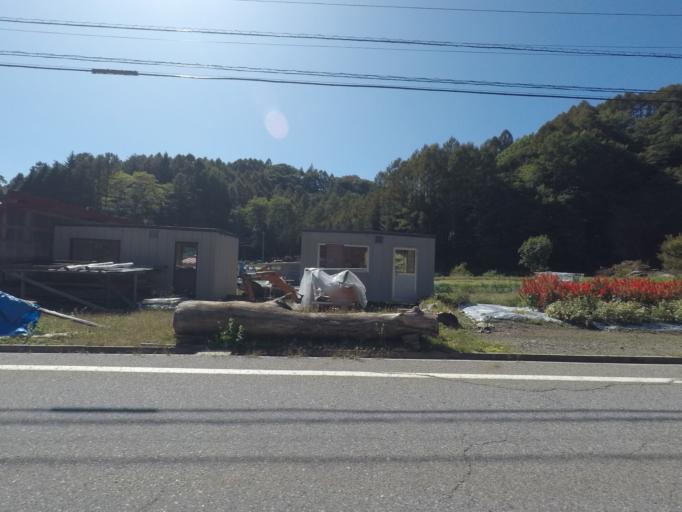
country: JP
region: Nagano
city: Shiojiri
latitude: 35.9826
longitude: 137.7435
